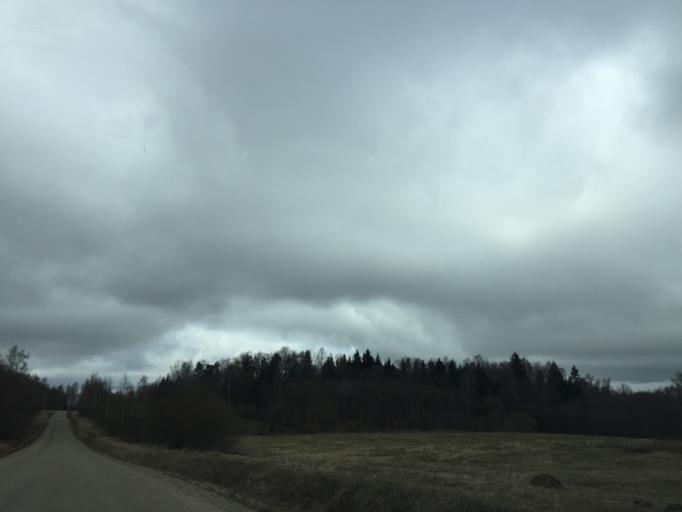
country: LV
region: Ilukste
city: Ilukste
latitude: 56.0507
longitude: 26.1851
